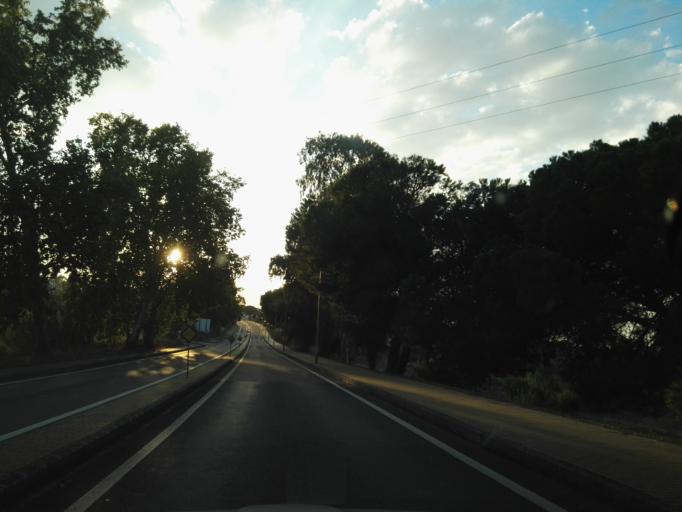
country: PT
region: Evora
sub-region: Mora
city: Mora
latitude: 38.9458
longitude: -8.1482
